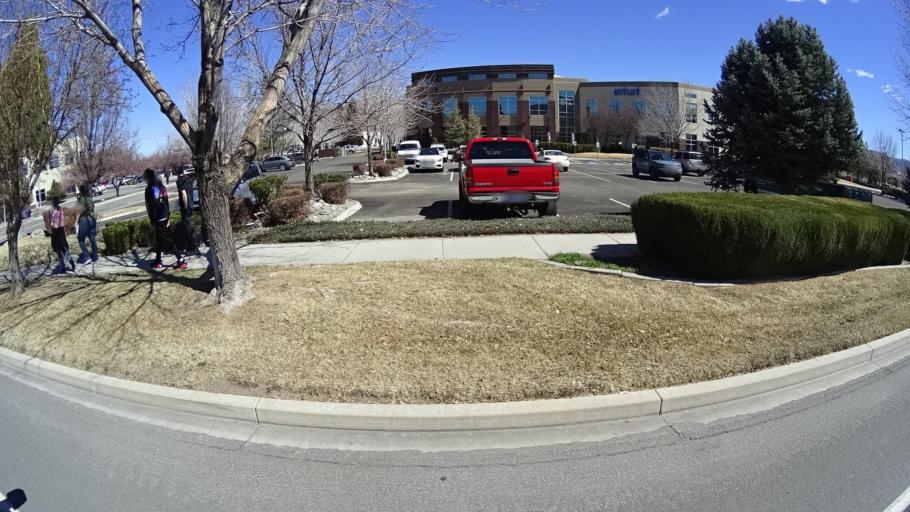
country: US
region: Nevada
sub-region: Washoe County
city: Reno
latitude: 39.4648
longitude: -119.7780
